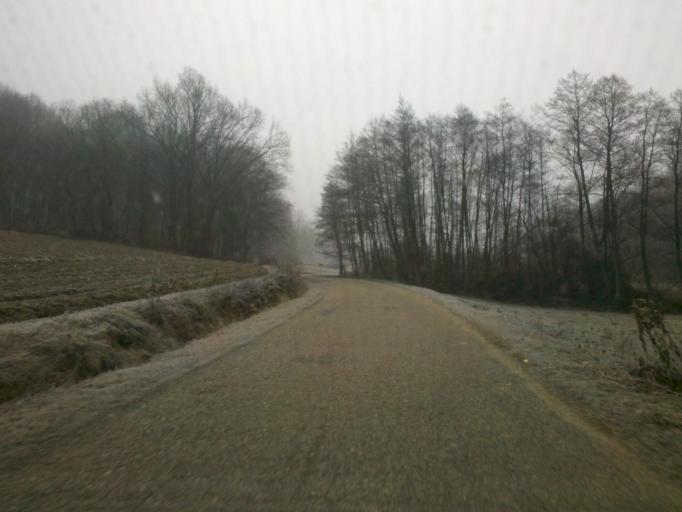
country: HR
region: Varazdinska
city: Ludbreg
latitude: 46.1683
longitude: 16.6265
